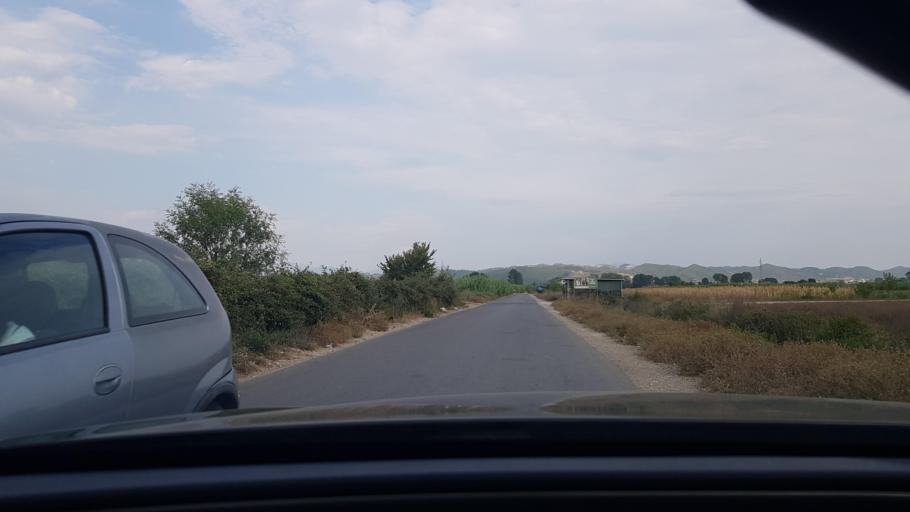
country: AL
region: Durres
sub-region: Rrethi i Durresit
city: Manze
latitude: 41.4837
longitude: 19.5331
